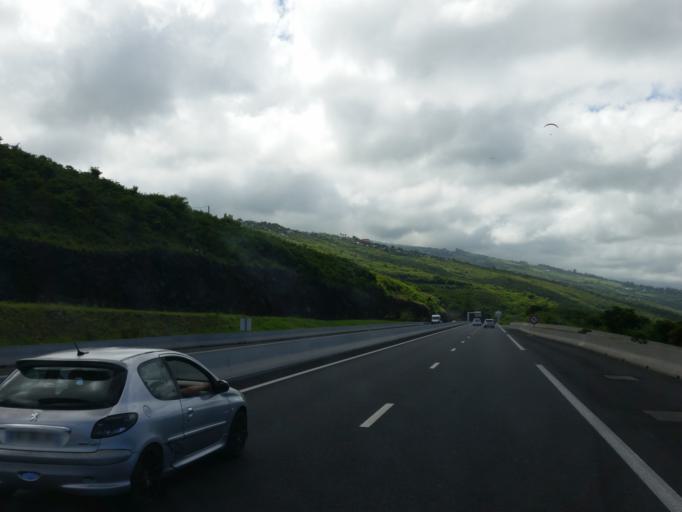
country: RE
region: Reunion
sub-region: Reunion
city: Trois-Bassins
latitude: -21.1012
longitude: 55.2677
